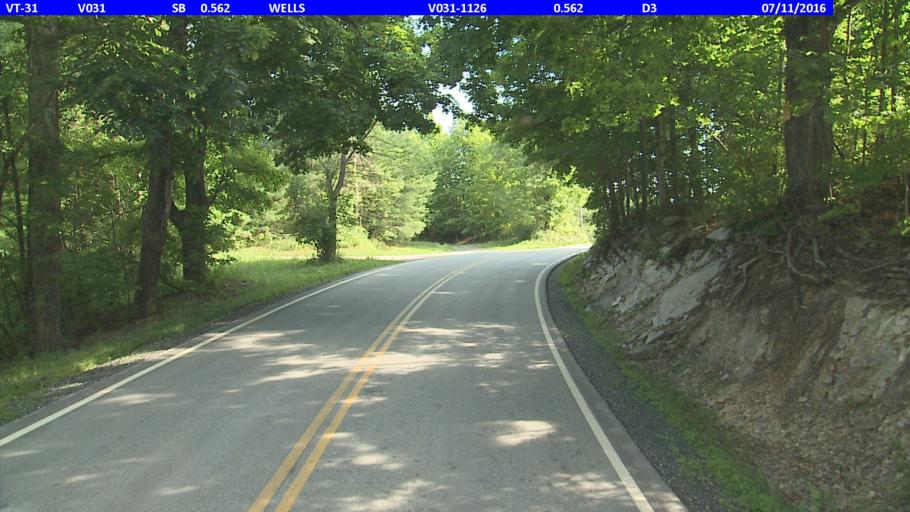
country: US
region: New York
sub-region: Washington County
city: Granville
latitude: 43.4457
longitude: -73.2459
